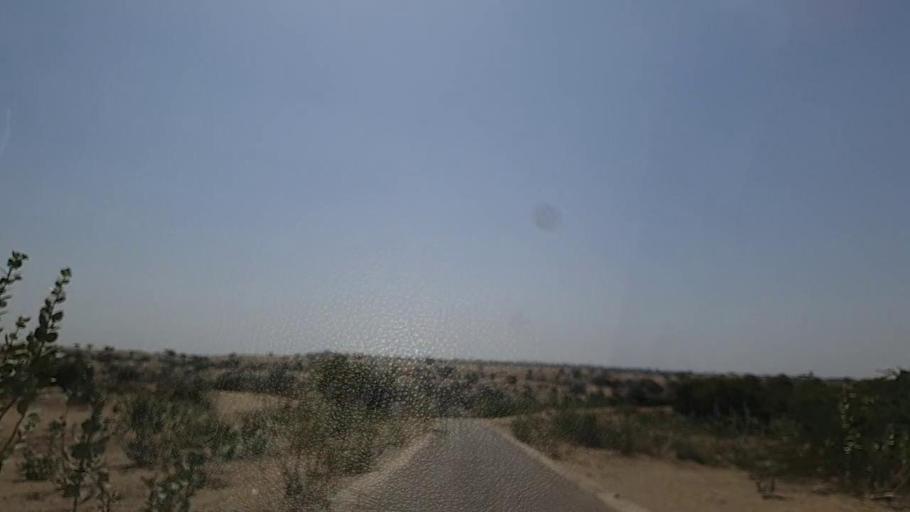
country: PK
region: Sindh
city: Mithi
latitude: 24.7061
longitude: 69.5911
